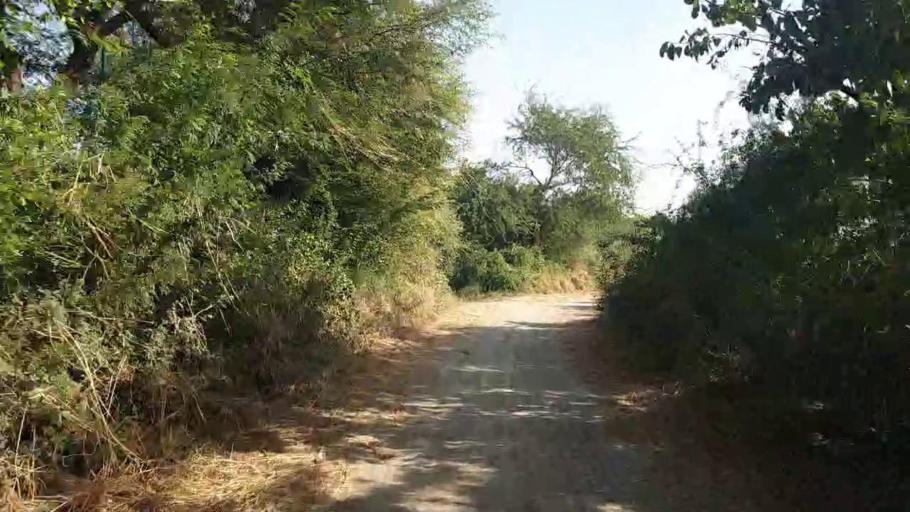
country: PK
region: Sindh
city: Matli
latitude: 25.0213
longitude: 68.7378
